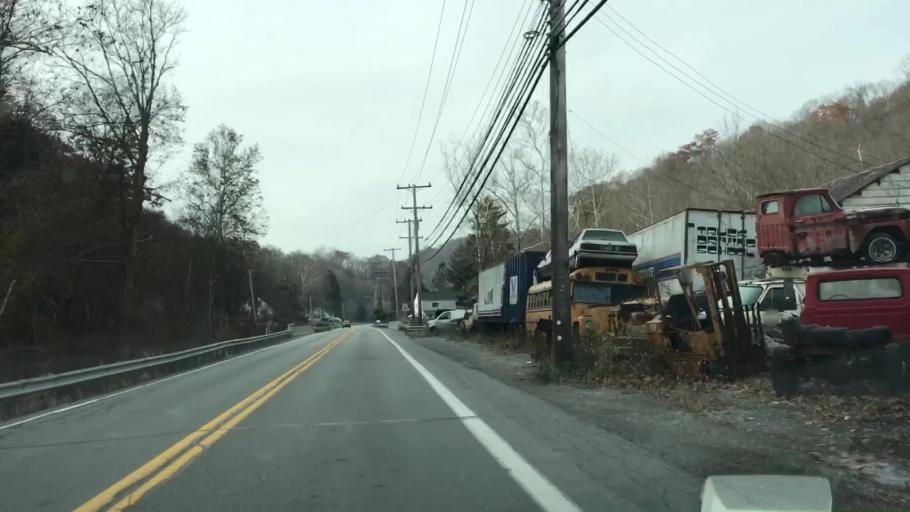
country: US
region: Pennsylvania
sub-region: Allegheny County
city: Carnot-Moon
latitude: 40.5383
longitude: -80.2218
